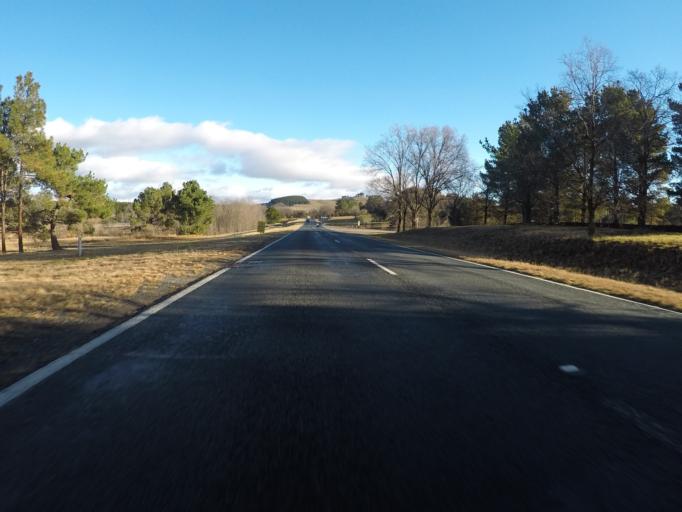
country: AU
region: Australian Capital Territory
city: Acton
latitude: -35.3072
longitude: 149.0754
